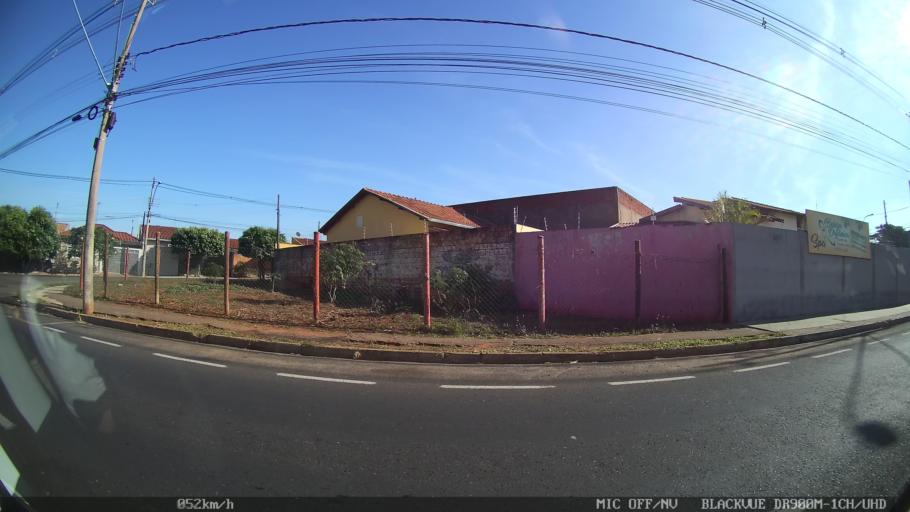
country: BR
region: Sao Paulo
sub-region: Sao Jose Do Rio Preto
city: Sao Jose do Rio Preto
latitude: -20.7707
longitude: -49.3916
